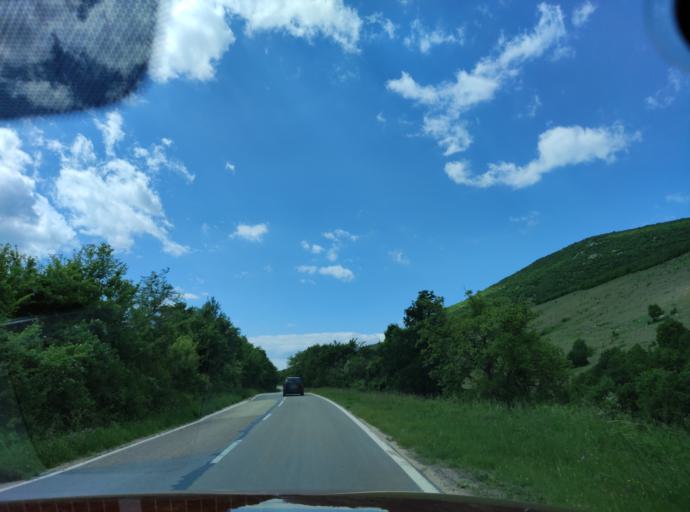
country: BG
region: Montana
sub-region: Obshtina Chiprovtsi
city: Chiprovtsi
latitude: 43.4757
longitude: 22.8422
